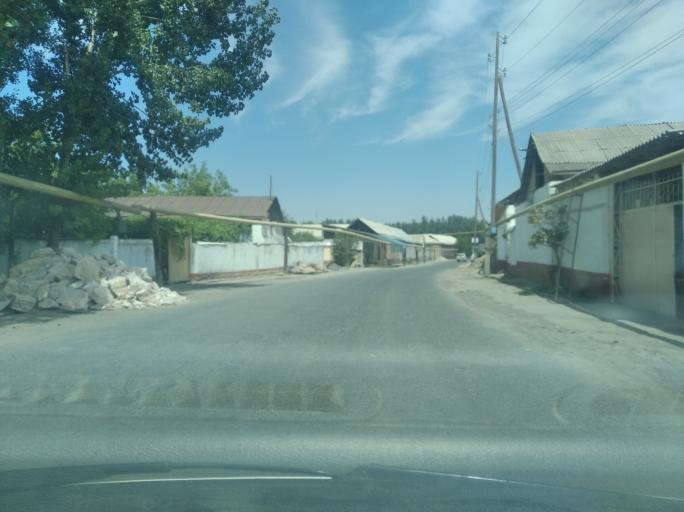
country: UZ
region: Andijon
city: Khujaobod
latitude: 40.6345
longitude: 72.4491
